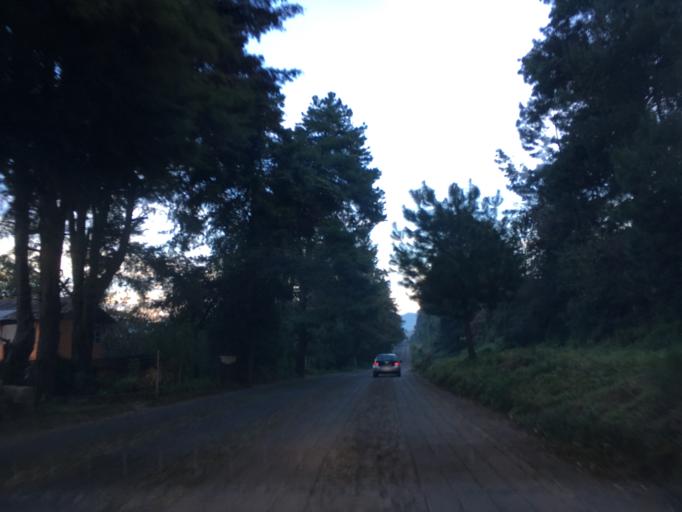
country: MX
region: Michoacan
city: Villa Escalante
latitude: 19.4147
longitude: -101.6730
